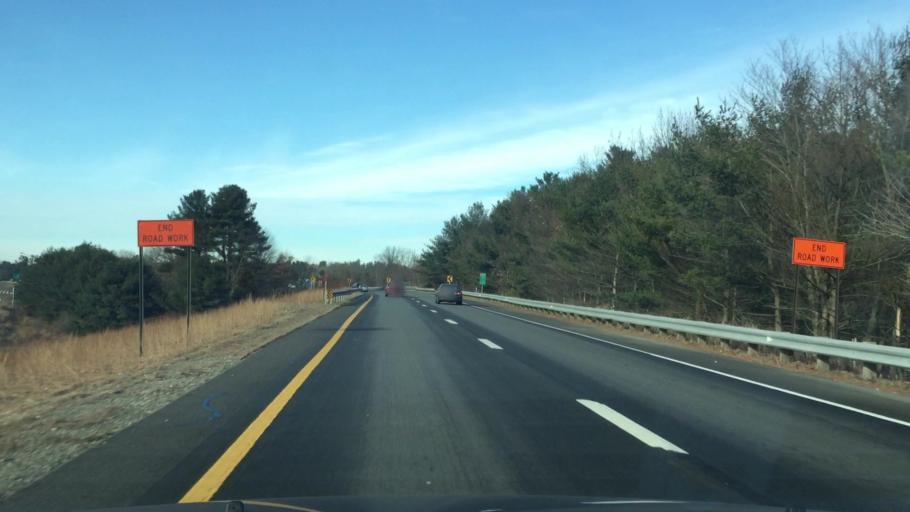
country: US
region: New Hampshire
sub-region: Hillsborough County
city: Manchester
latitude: 42.9613
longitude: -71.4134
